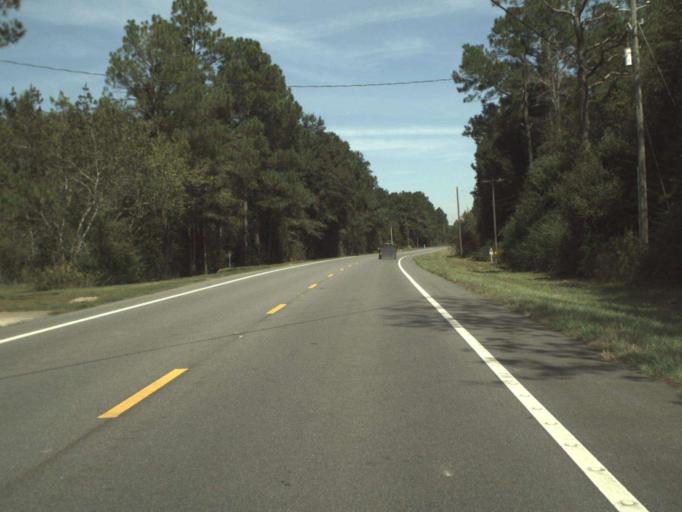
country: US
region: Florida
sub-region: Washington County
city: Chipley
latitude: 30.8109
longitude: -85.5340
